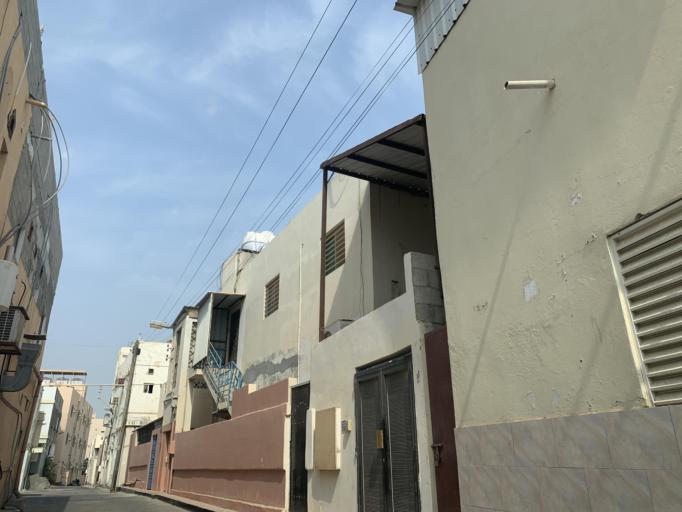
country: BH
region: Manama
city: Jidd Hafs
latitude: 26.2096
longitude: 50.4876
